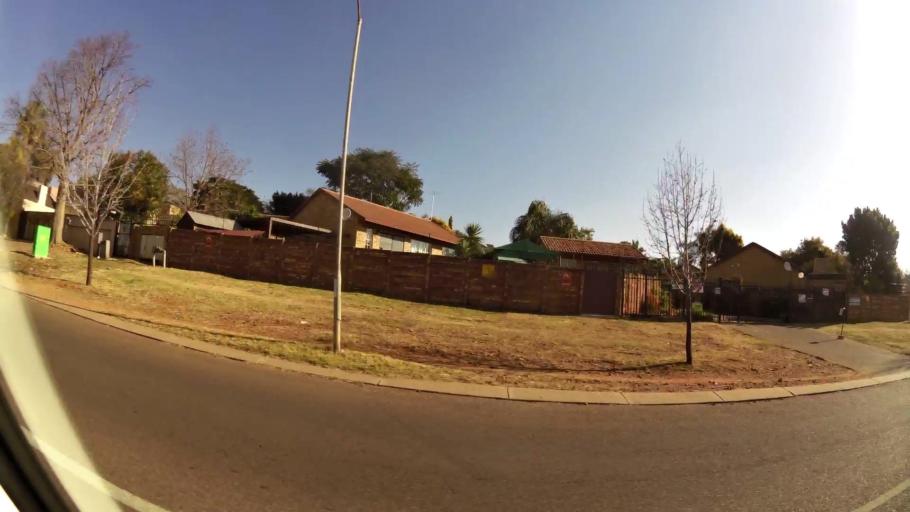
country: ZA
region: Gauteng
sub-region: City of Tshwane Metropolitan Municipality
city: Centurion
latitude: -25.8326
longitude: 28.2988
